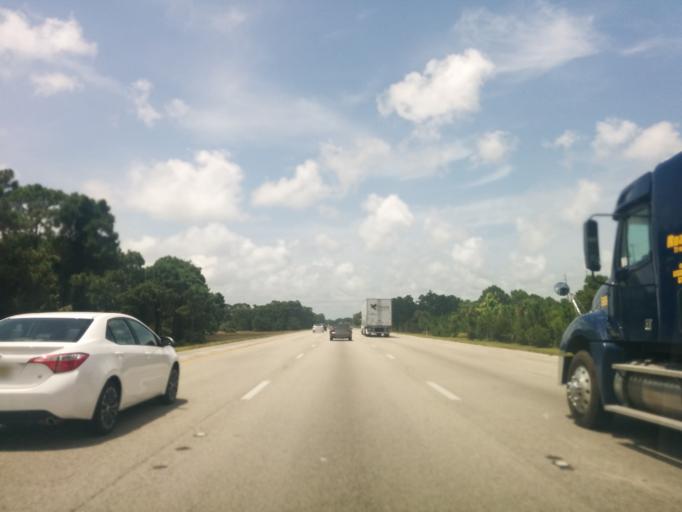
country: US
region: Florida
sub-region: Saint Lucie County
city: River Park
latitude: 27.3180
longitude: -80.4135
